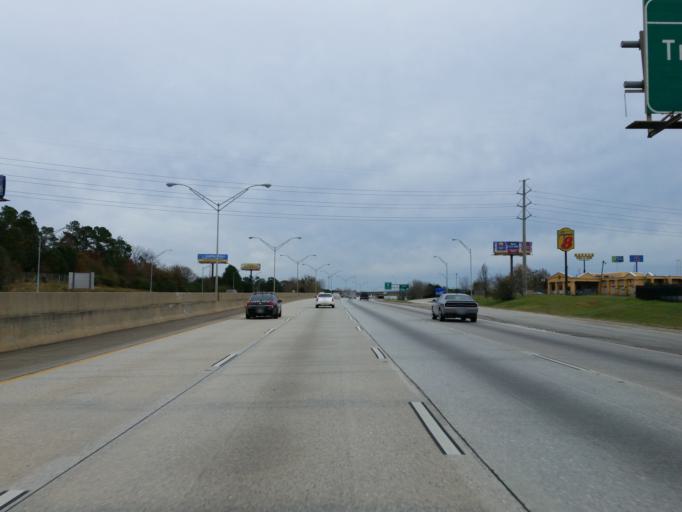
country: US
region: Georgia
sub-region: Monroe County
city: Forsyth
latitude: 33.0371
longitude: -83.9265
